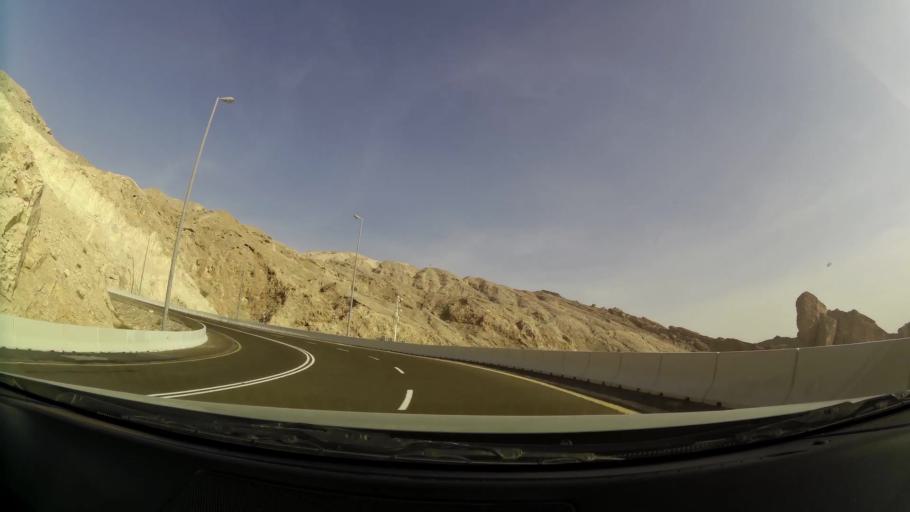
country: AE
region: Abu Dhabi
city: Al Ain
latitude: 24.0935
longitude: 55.7570
